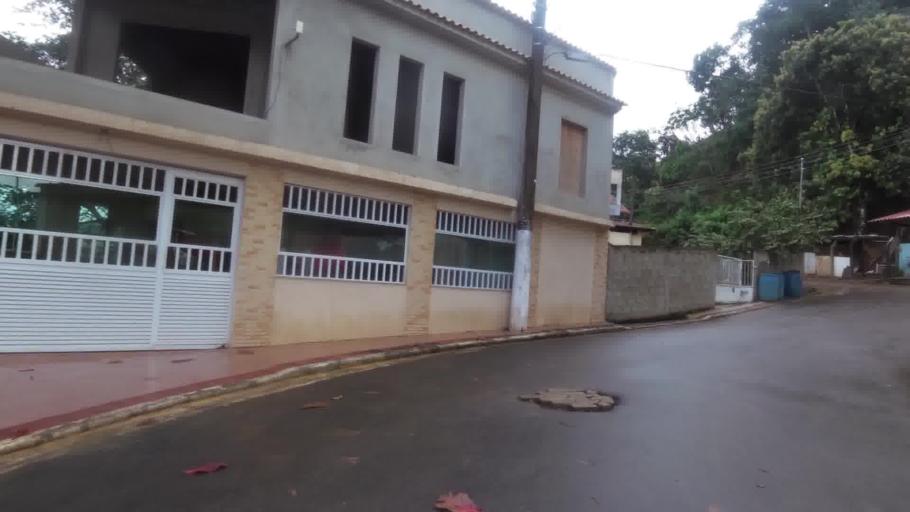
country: BR
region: Espirito Santo
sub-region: Alfredo Chaves
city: Alfredo Chaves
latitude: -20.6856
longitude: -40.6797
